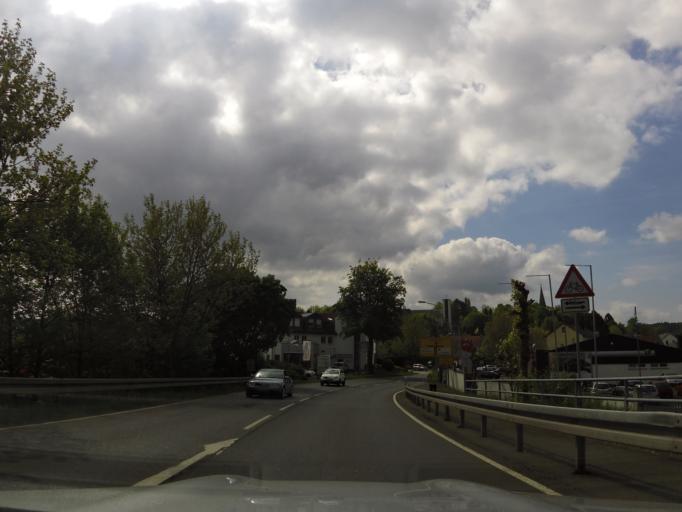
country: DE
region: Hesse
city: Burgsolms
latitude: 50.5439
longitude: 8.4088
